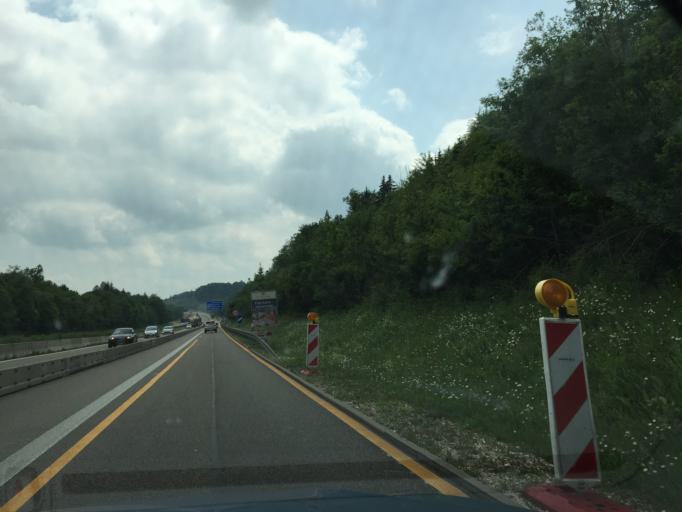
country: DE
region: Baden-Wuerttemberg
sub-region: Regierungsbezirk Stuttgart
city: Nattheim
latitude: 48.6965
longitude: 10.2148
